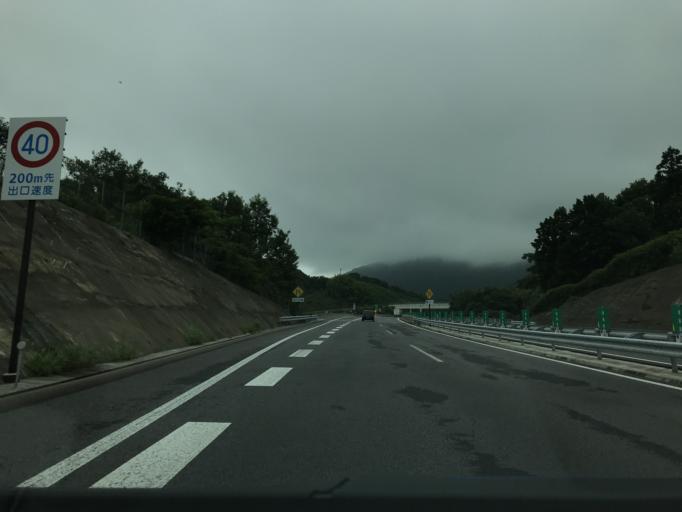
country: JP
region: Oita
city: Bungo-Takada-shi
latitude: 33.5004
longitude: 131.3155
